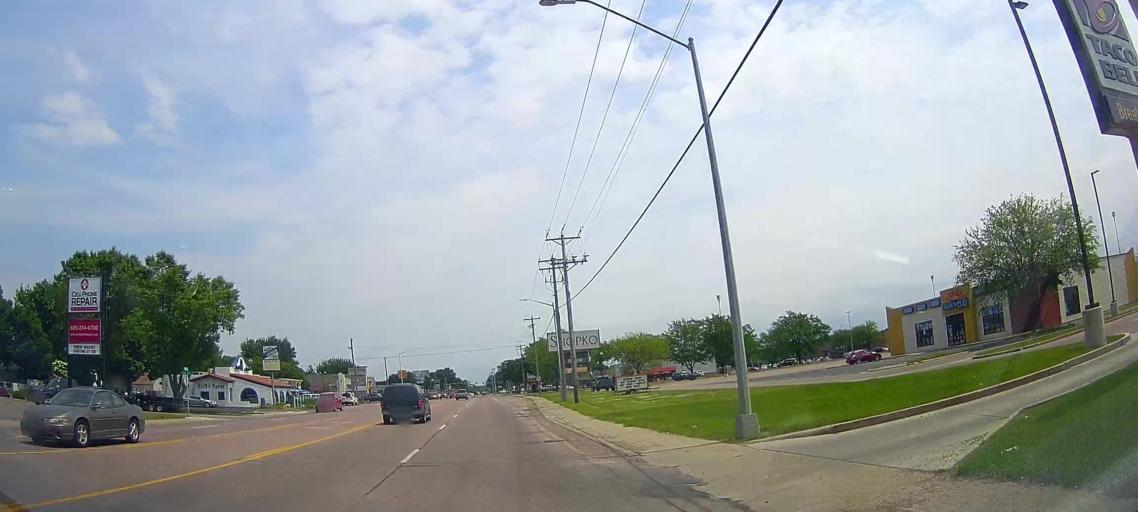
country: US
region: South Dakota
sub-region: Minnehaha County
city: Sioux Falls
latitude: 43.5148
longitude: -96.7452
